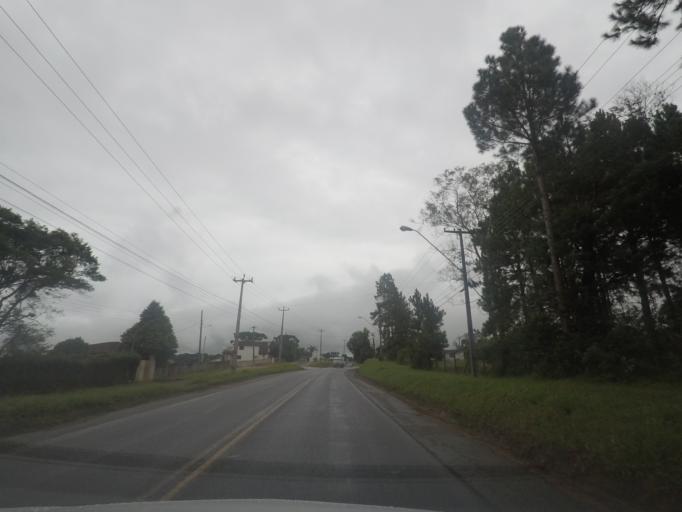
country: BR
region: Parana
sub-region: Quatro Barras
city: Quatro Barras
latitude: -25.3317
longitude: -49.0786
